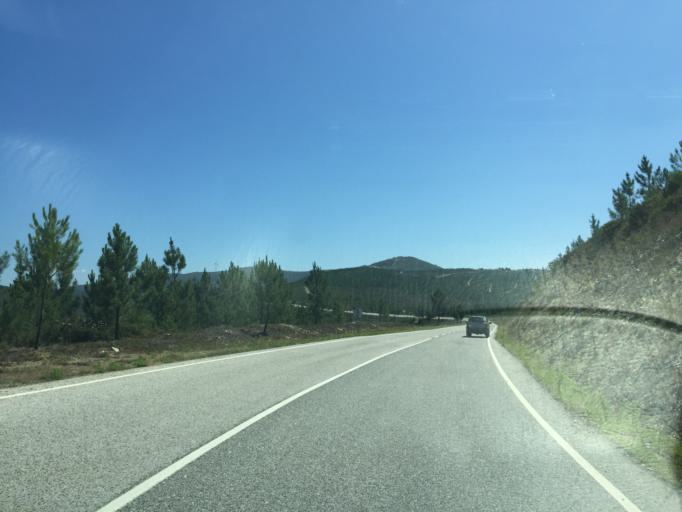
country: PT
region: Coimbra
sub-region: Pampilhosa da Serra
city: Pampilhosa da Serra
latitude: 40.1193
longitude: -7.8261
